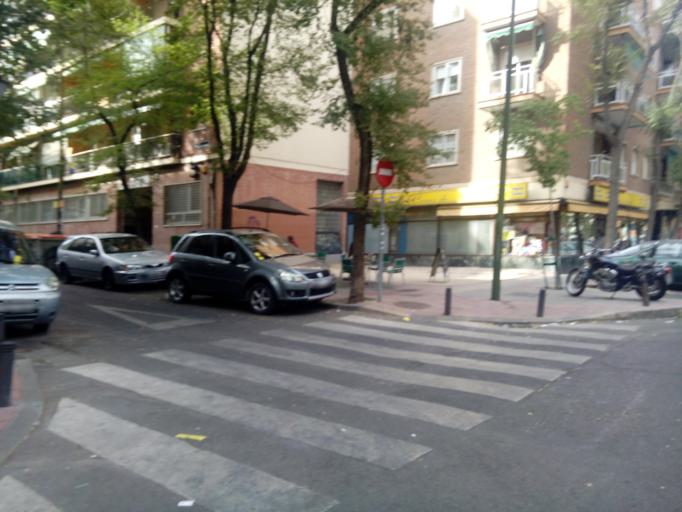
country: ES
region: Madrid
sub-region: Provincia de Madrid
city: Usera
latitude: 40.3919
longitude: -3.7097
